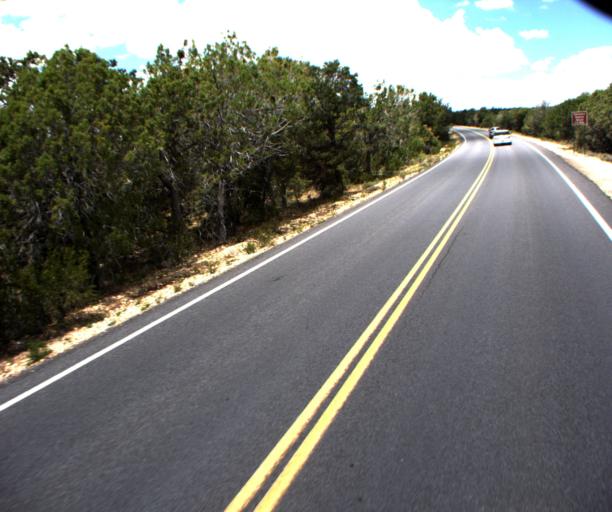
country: US
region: Arizona
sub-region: Coconino County
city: Grand Canyon
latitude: 36.0279
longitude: -111.8276
